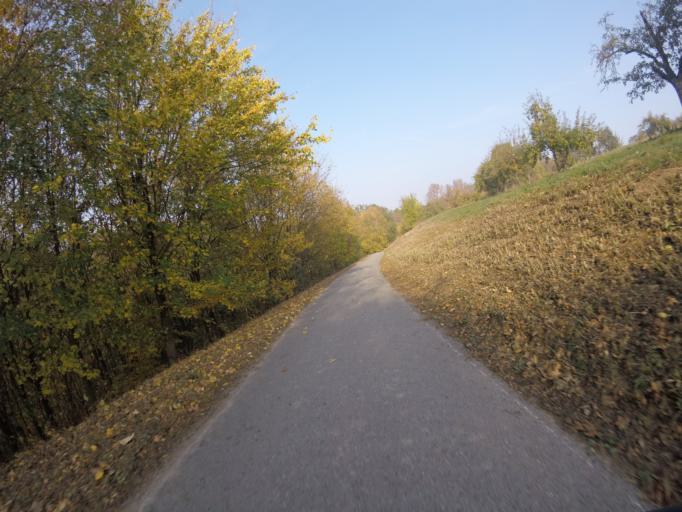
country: DE
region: Baden-Wuerttemberg
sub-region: Regierungsbezirk Stuttgart
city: Mittelschontal
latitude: 48.9435
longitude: 9.3999
